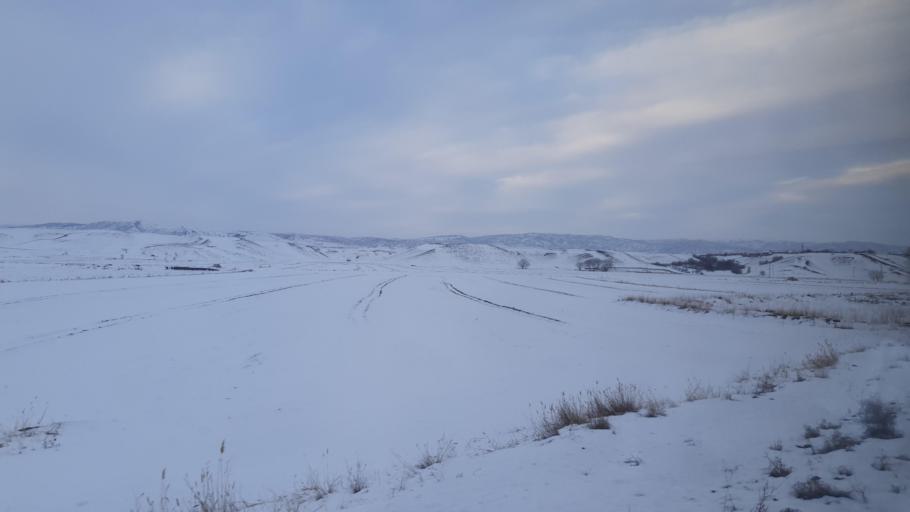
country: TR
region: Kirsehir
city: Mecidiye
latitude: 39.6860
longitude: 34.4028
